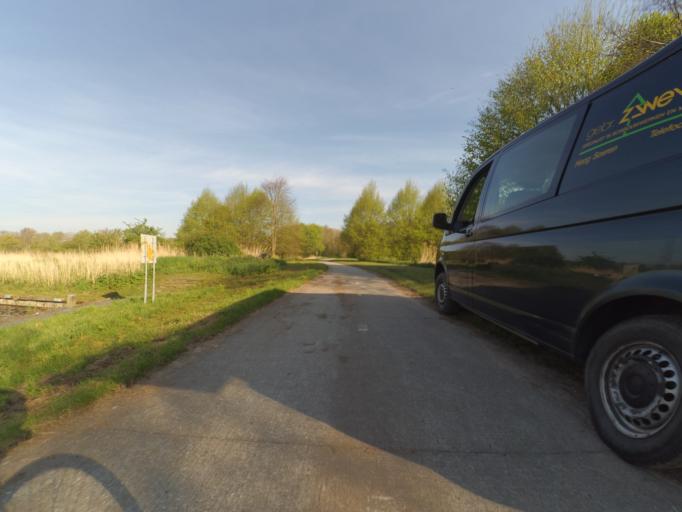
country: NL
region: North Holland
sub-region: Gemeente Huizen
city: Huizen
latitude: 52.3461
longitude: 5.2849
